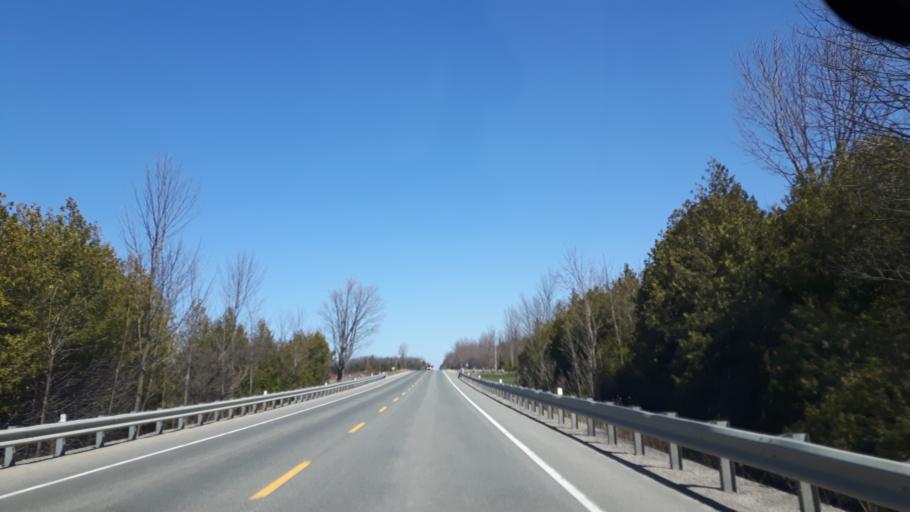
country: CA
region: Ontario
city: Goderich
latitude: 43.6538
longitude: -81.7060
